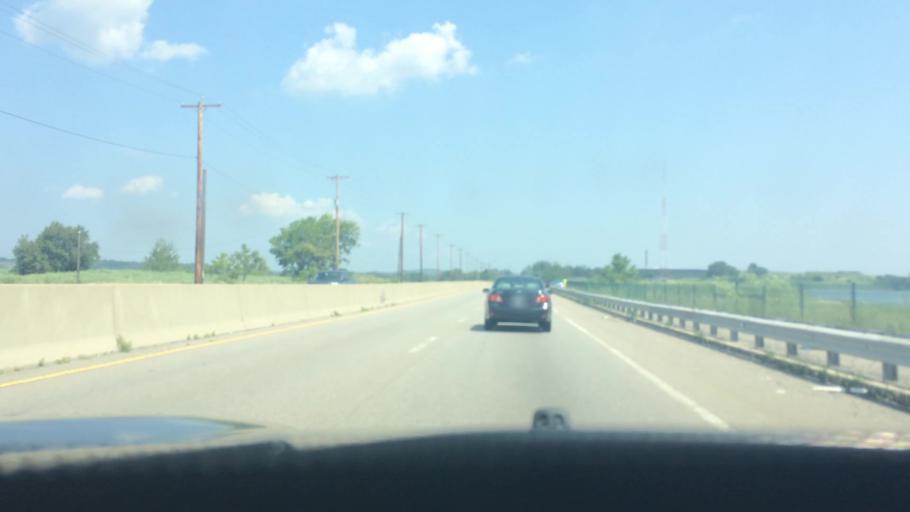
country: US
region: Massachusetts
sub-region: Suffolk County
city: Revere
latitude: 42.4316
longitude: -70.9968
